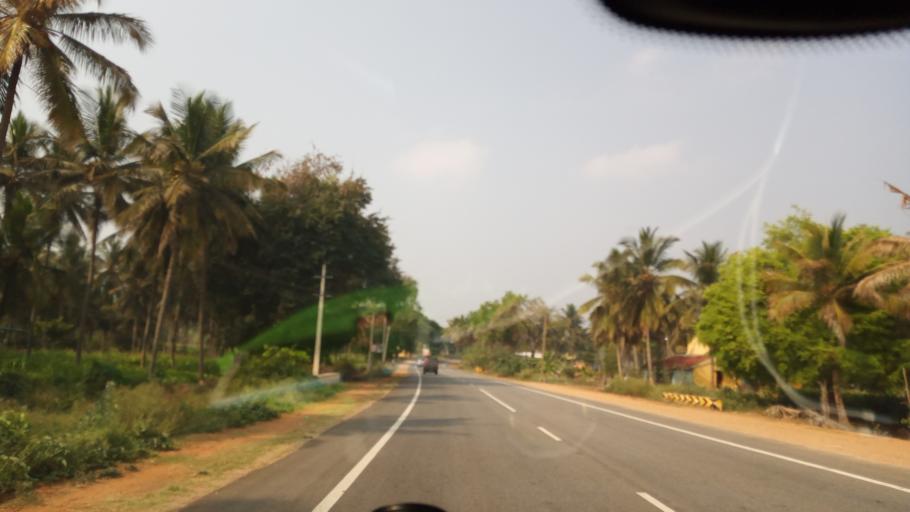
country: IN
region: Karnataka
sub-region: Mandya
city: Nagamangala
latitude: 12.7622
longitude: 76.7348
